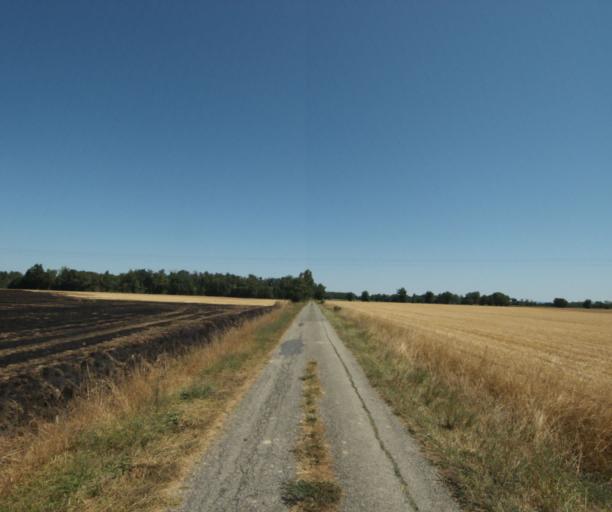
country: FR
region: Midi-Pyrenees
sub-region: Departement de la Haute-Garonne
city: Revel
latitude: 43.4855
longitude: 1.9580
